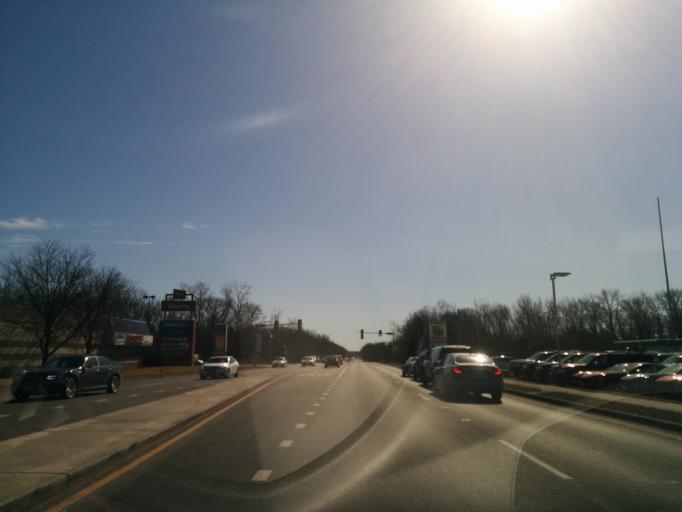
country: US
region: Illinois
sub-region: Cook County
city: Countryside
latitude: 41.7772
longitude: -87.8682
